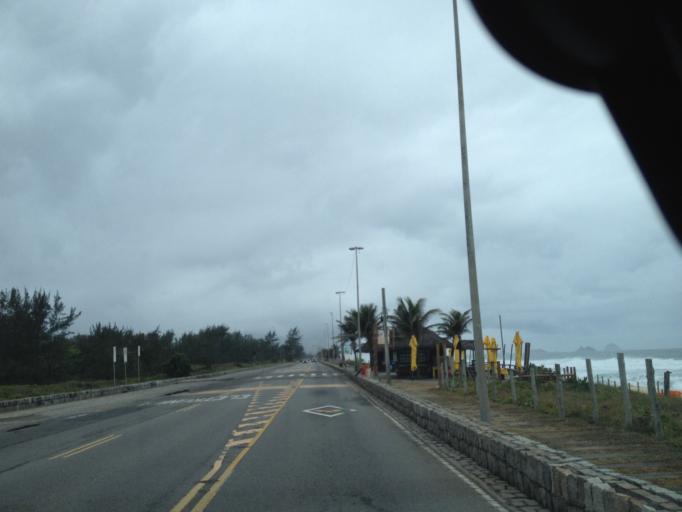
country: BR
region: Rio de Janeiro
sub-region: Nilopolis
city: Nilopolis
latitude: -23.0149
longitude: -43.4064
